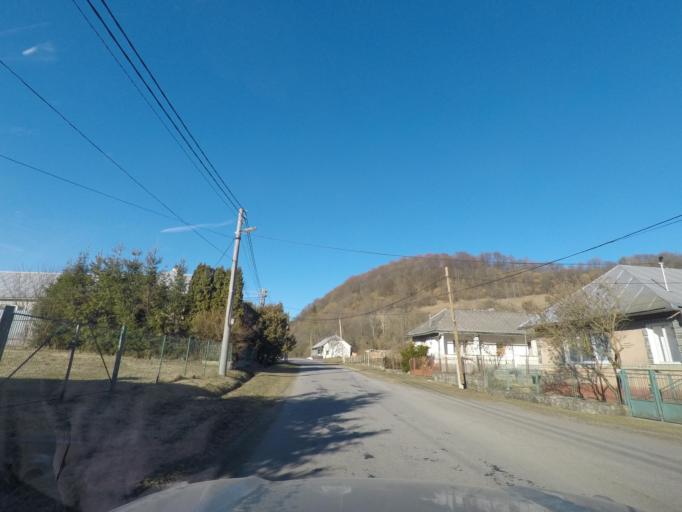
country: SK
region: Presovsky
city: Medzilaborce
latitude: 49.1660
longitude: 22.0382
